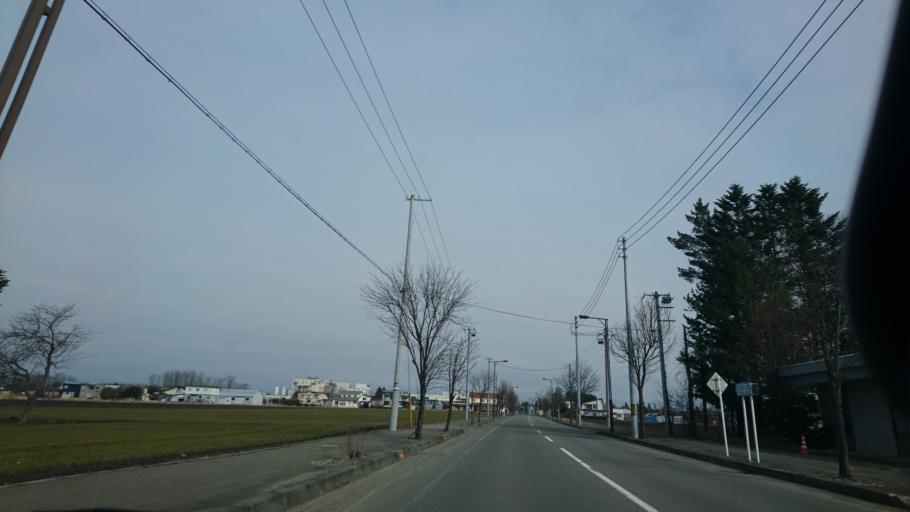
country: JP
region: Hokkaido
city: Otofuke
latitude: 42.9730
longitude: 143.2123
